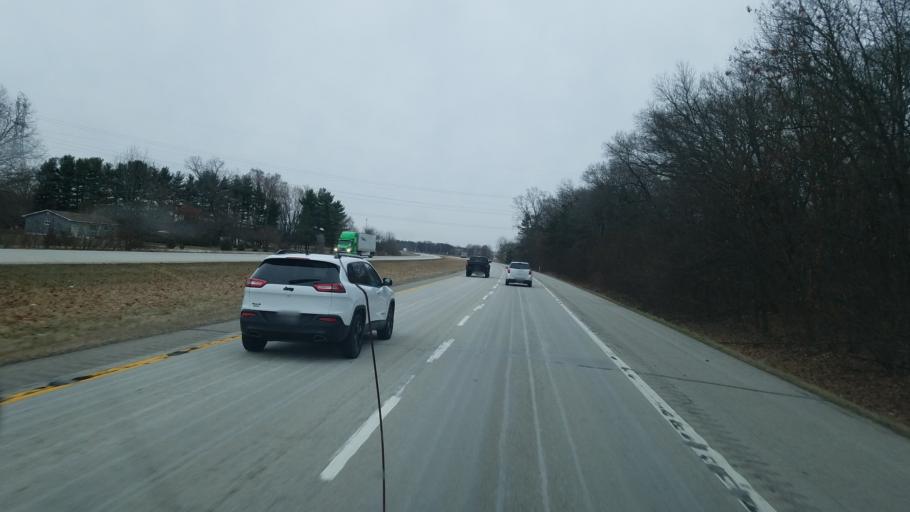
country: US
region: Indiana
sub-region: Starke County
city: Koontz Lake
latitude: 41.3822
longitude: -86.5688
